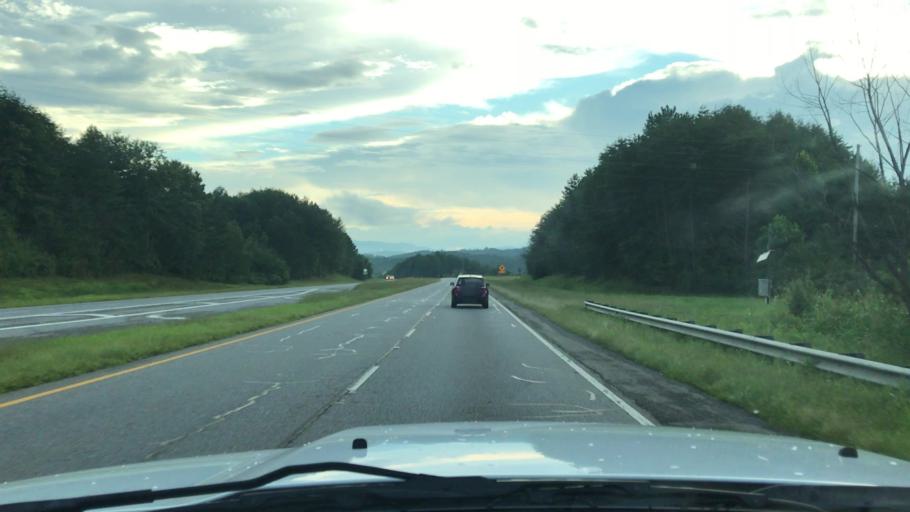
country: US
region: Georgia
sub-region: Fannin County
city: Blue Ridge
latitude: 34.8923
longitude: -84.2751
